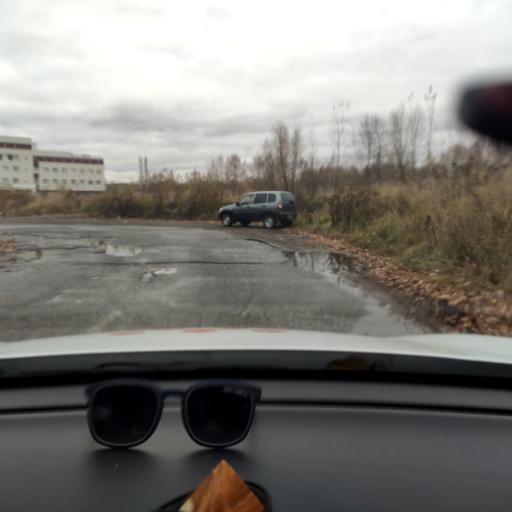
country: RU
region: Tatarstan
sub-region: Gorod Kazan'
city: Kazan
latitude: 55.8522
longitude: 49.1331
